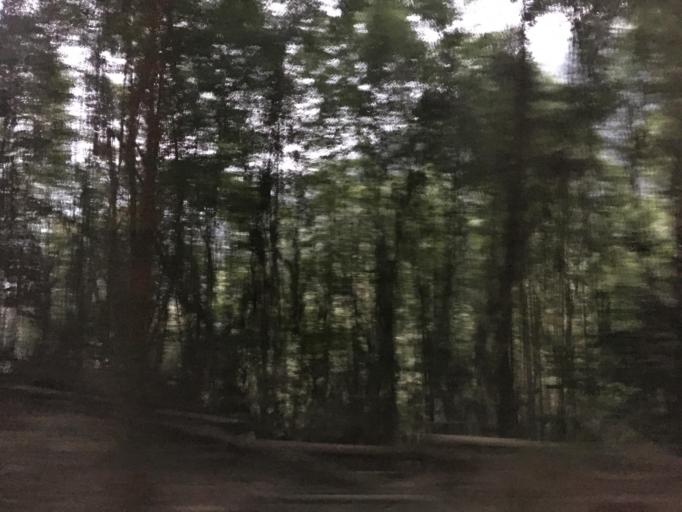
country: TW
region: Taiwan
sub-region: Chiayi
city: Jiayi Shi
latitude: 23.5188
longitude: 120.6546
